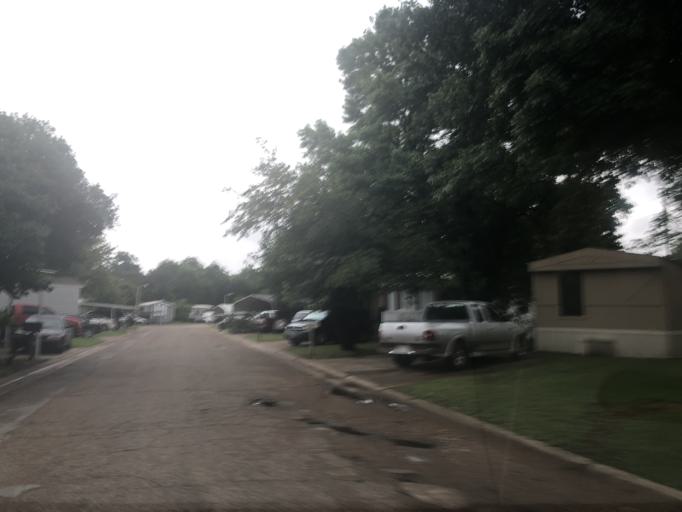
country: US
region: Texas
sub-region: Dallas County
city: Irving
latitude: 32.7924
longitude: -96.9568
